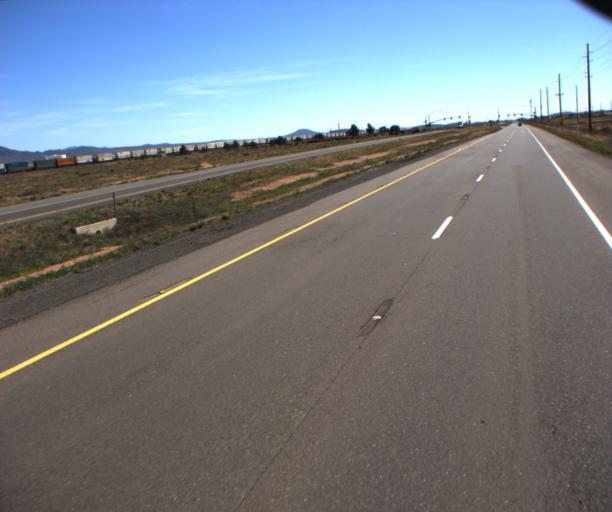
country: US
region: Arizona
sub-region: Mohave County
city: New Kingman-Butler
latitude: 35.2735
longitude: -113.9570
